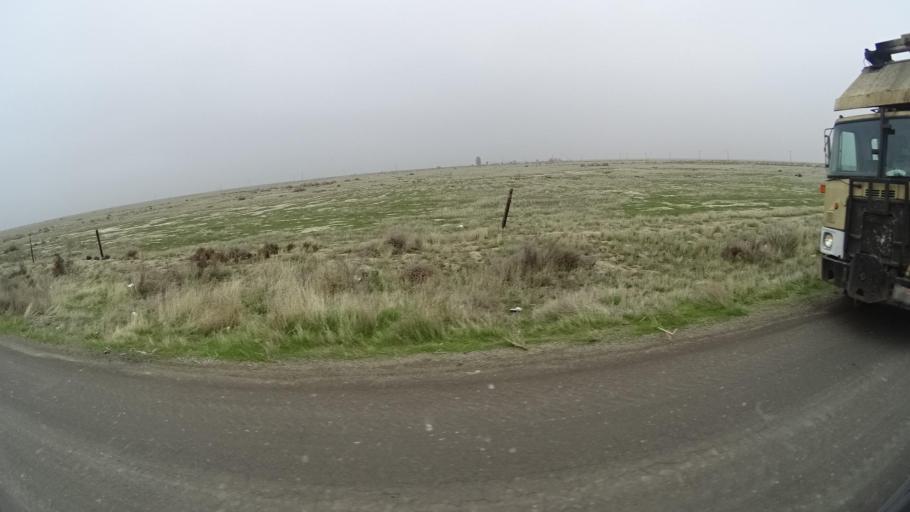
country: US
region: California
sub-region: Tulare County
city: Alpaugh
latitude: 35.7201
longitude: -119.4727
